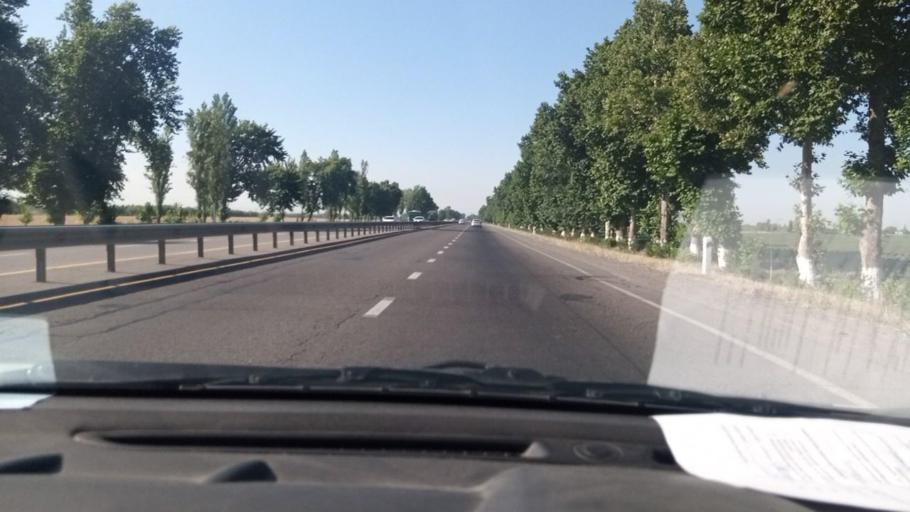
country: UZ
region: Toshkent Shahri
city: Bektemir
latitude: 41.2041
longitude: 69.4028
